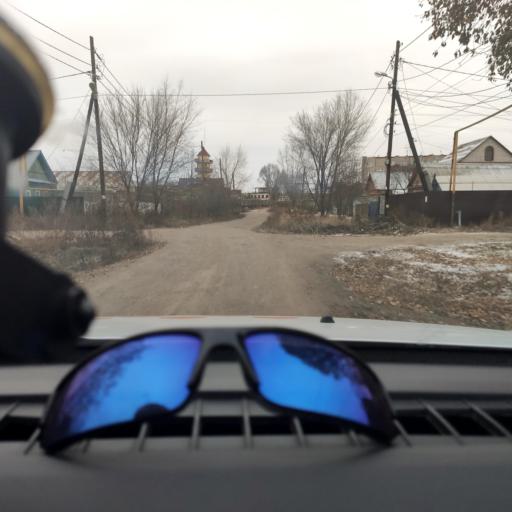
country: RU
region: Samara
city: Samara
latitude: 53.1337
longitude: 50.1024
